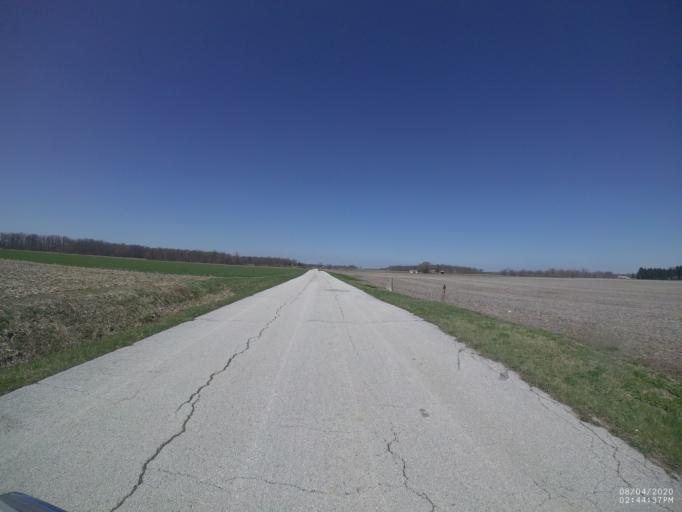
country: US
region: Ohio
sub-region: Sandusky County
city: Gibsonburg
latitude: 41.2941
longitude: -83.2956
